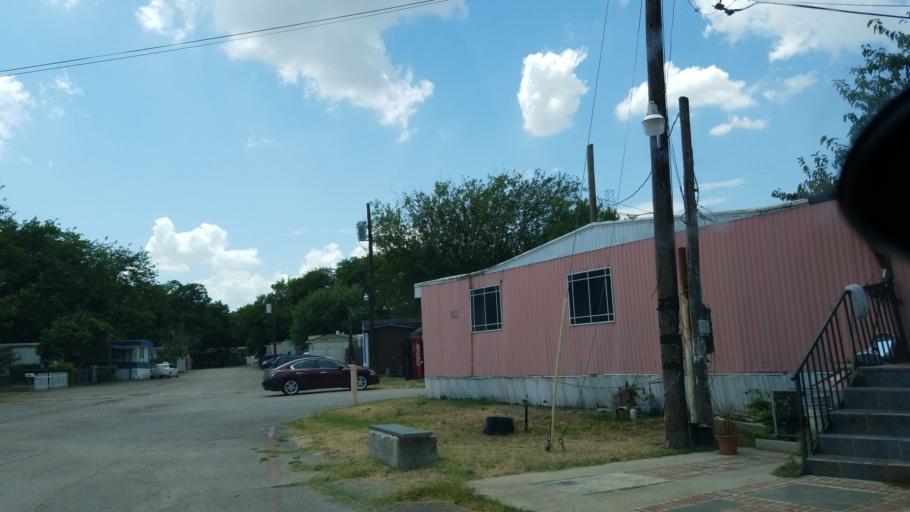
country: US
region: Texas
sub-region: Dallas County
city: Cockrell Hill
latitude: 32.7483
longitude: -96.8850
